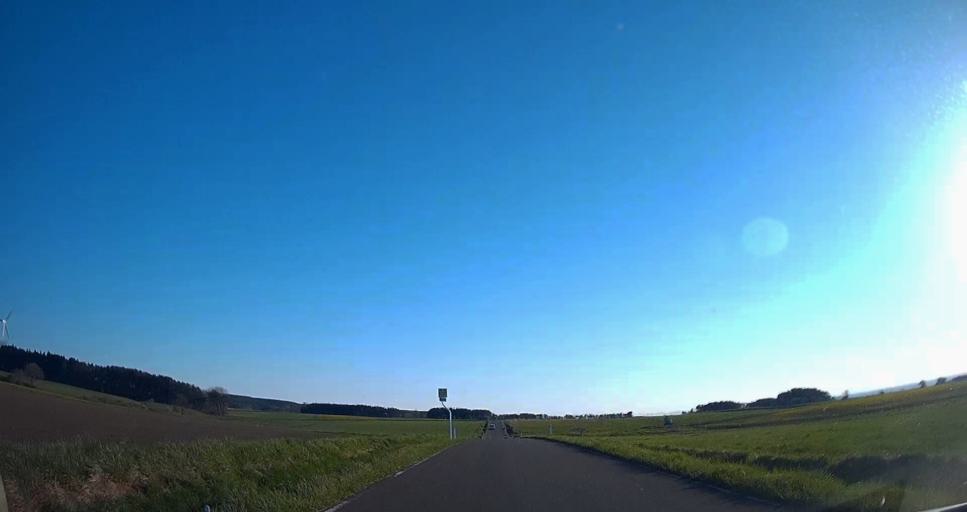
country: JP
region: Aomori
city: Mutsu
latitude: 41.1189
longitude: 141.2771
